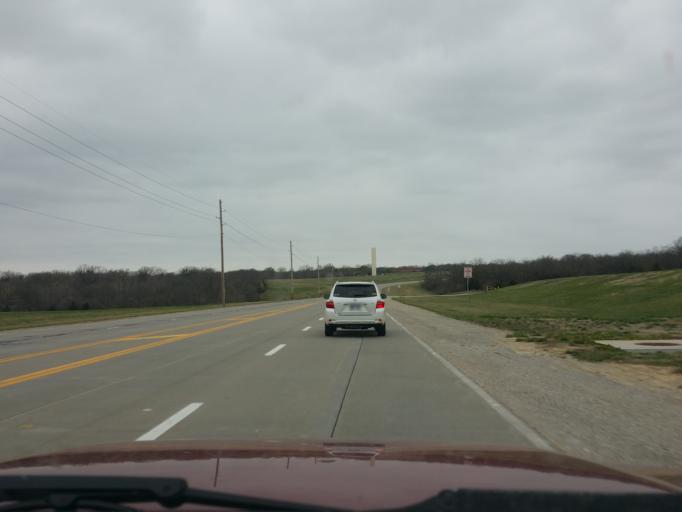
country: US
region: Kansas
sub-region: Wyandotte County
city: Edwardsville
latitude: 39.1095
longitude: -94.8414
